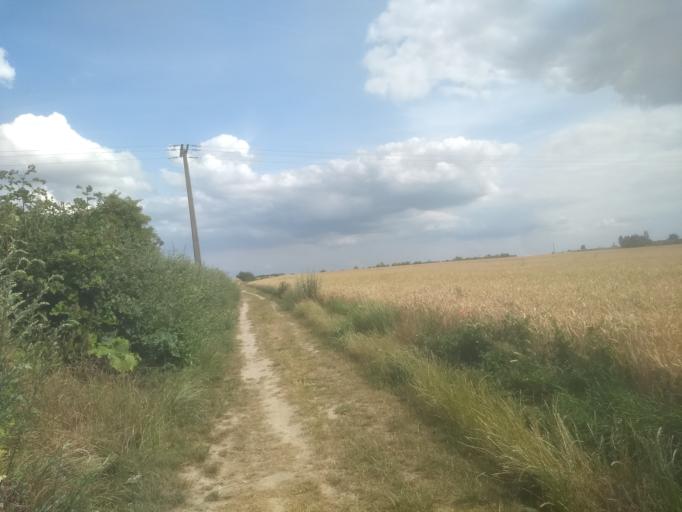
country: FR
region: Nord-Pas-de-Calais
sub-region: Departement du Pas-de-Calais
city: Beaurains
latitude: 50.2761
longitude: 2.7942
